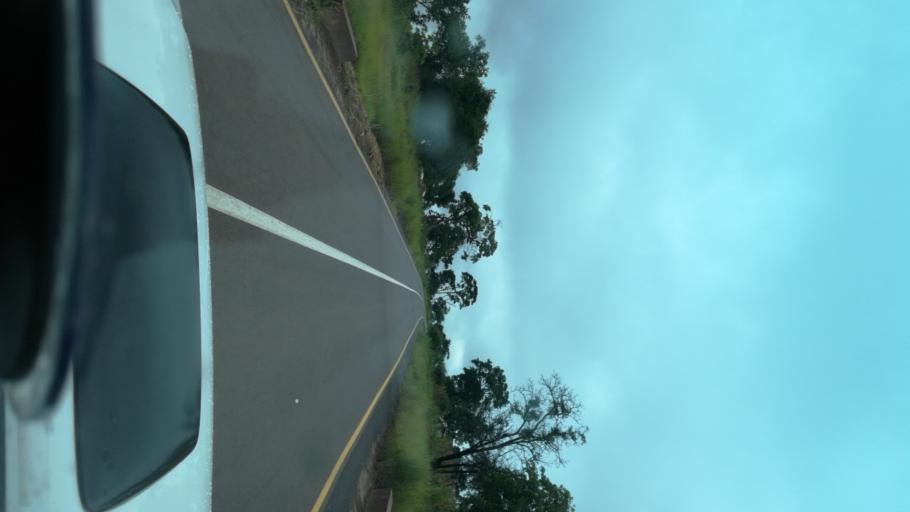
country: CD
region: Katanga
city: Lubumbashi
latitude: -11.0241
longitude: 28.0446
